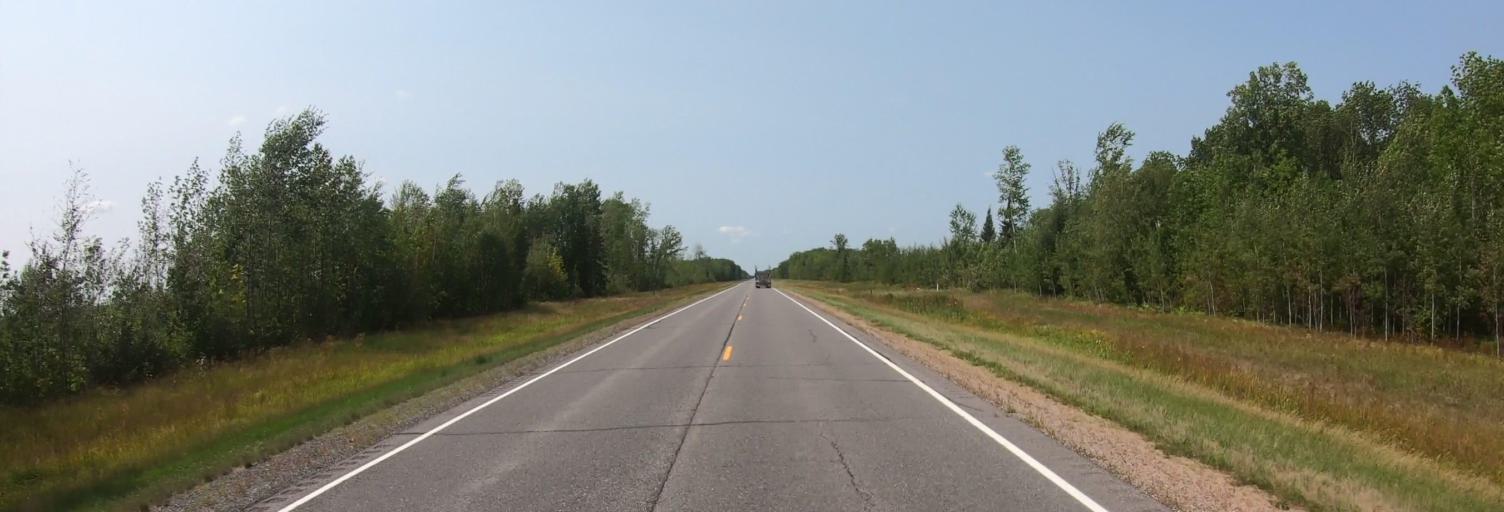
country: US
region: Minnesota
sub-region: Koochiching County
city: International Falls
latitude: 48.5127
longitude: -93.7380
